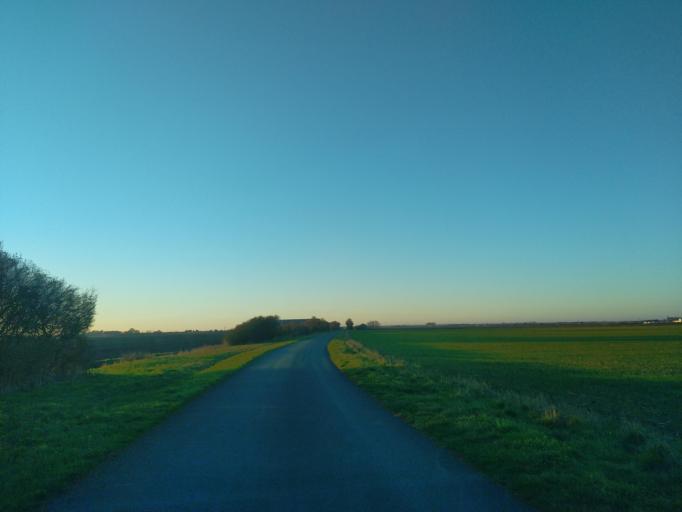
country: FR
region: Pays de la Loire
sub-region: Departement de la Vendee
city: Triaize
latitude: 46.3743
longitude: -1.2885
